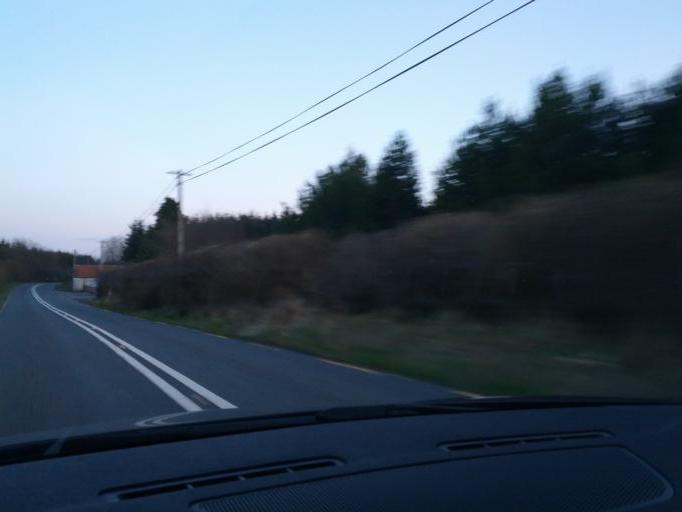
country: IE
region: Connaught
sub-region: Roscommon
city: Boyle
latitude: 53.9116
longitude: -8.2696
